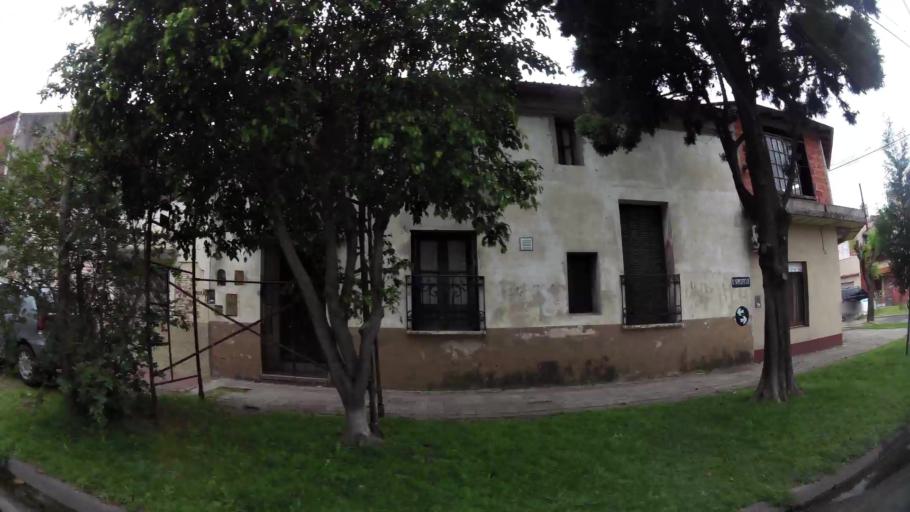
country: AR
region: Buenos Aires
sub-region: Partido de Avellaneda
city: Avellaneda
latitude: -34.6799
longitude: -58.3742
